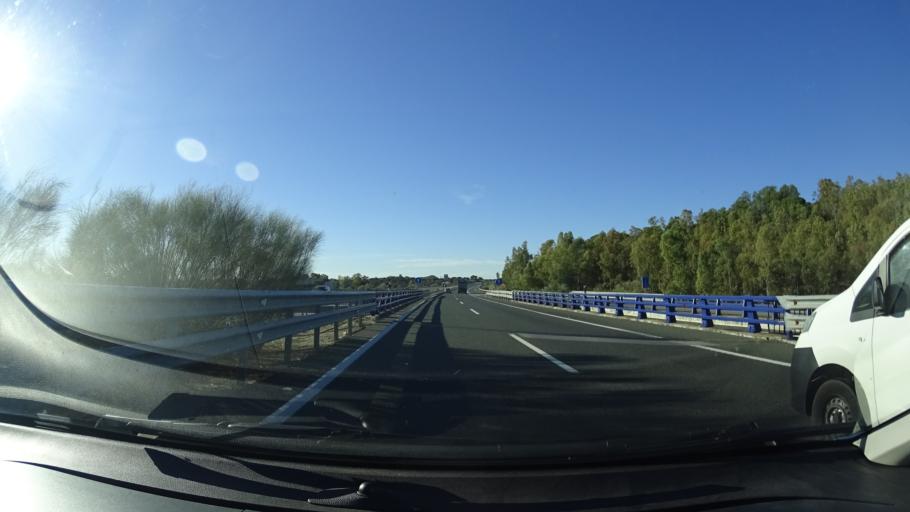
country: ES
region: Extremadura
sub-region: Provincia de Badajoz
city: Monesterio
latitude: 38.0285
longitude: -6.2224
